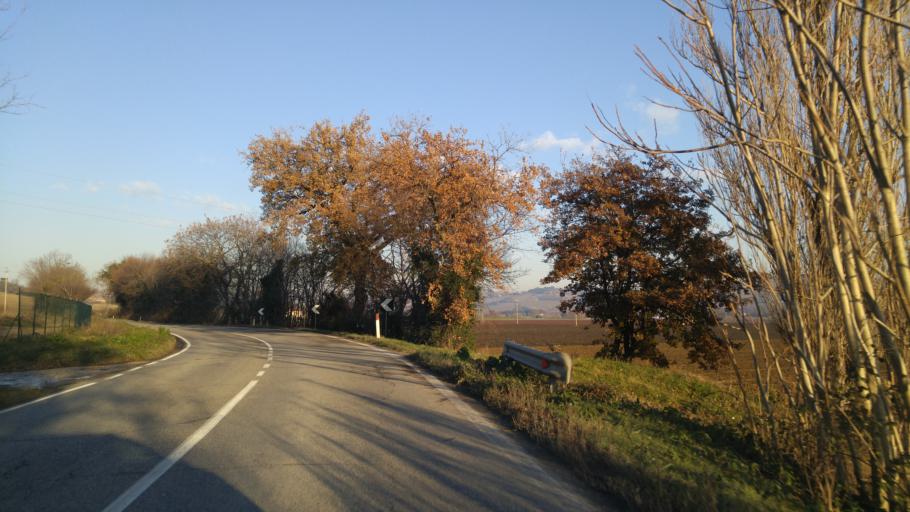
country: IT
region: The Marches
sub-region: Provincia di Pesaro e Urbino
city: Monte Porzio
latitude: 43.6804
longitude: 13.0311
